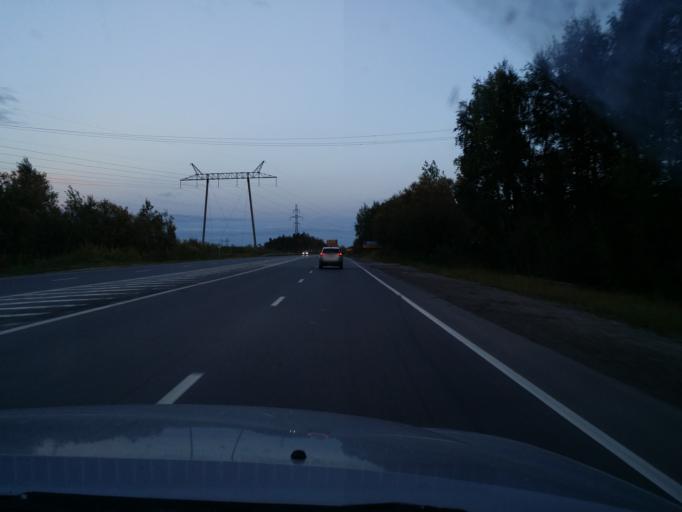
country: RU
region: Khanty-Mansiyskiy Avtonomnyy Okrug
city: Megion
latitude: 61.0480
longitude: 76.3418
